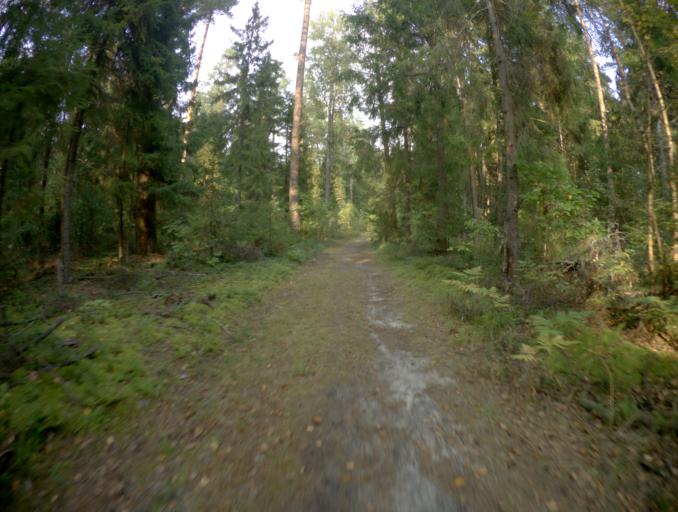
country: RU
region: Vladimir
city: Bogolyubovo
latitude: 56.0969
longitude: 40.5483
